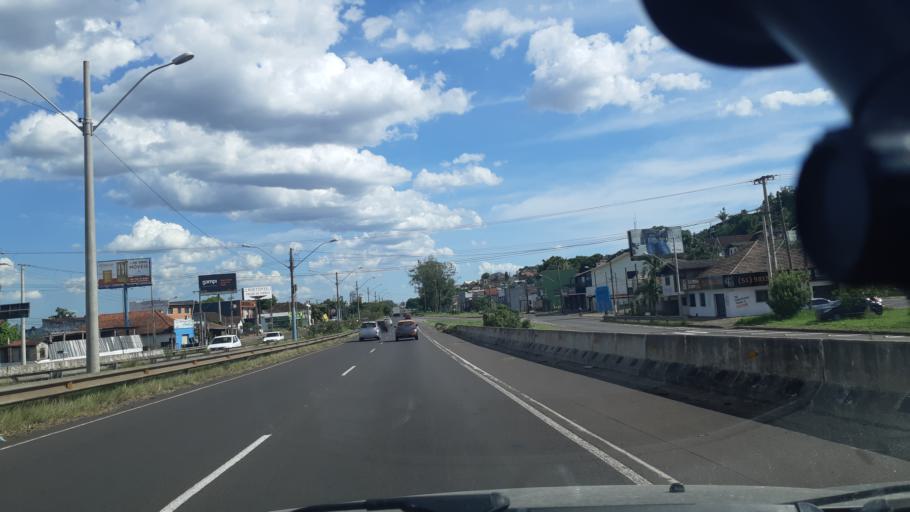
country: BR
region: Rio Grande do Sul
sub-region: Novo Hamburgo
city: Novo Hamburgo
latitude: -29.6717
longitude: -51.1430
